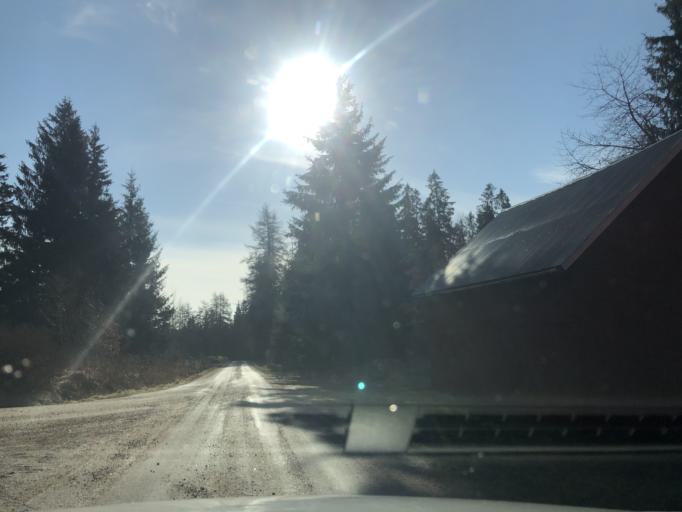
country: SE
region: Vaestra Goetaland
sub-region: Ulricehamns Kommun
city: Ulricehamn
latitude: 57.8090
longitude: 13.3843
